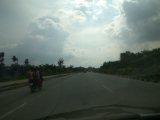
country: IN
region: Karnataka
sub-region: Kolar
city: Malur
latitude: 13.1308
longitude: 77.9646
